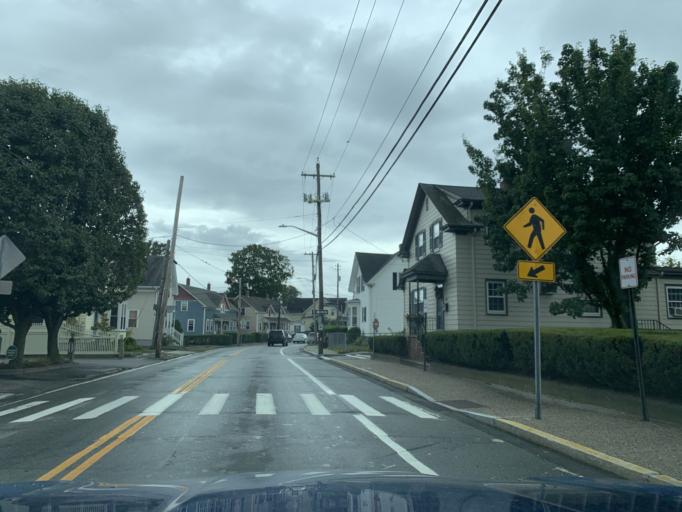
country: US
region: Rhode Island
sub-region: Bristol County
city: Warren
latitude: 41.7348
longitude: -71.2843
